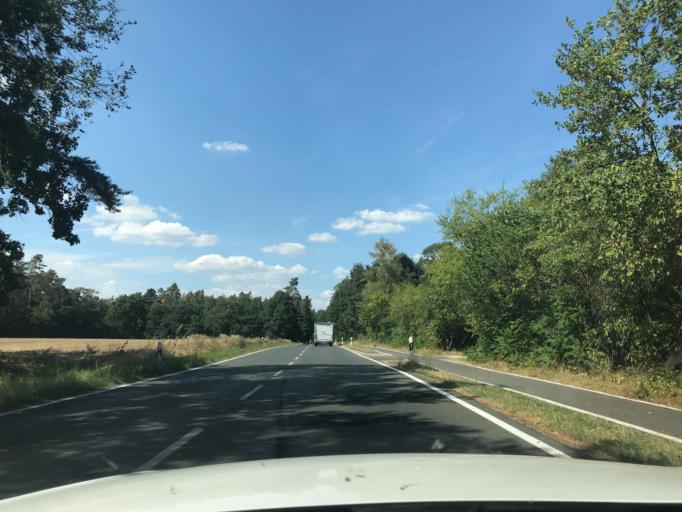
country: DE
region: Bavaria
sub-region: Regierungsbezirk Mittelfranken
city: Erlangen
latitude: 49.5558
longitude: 11.0162
